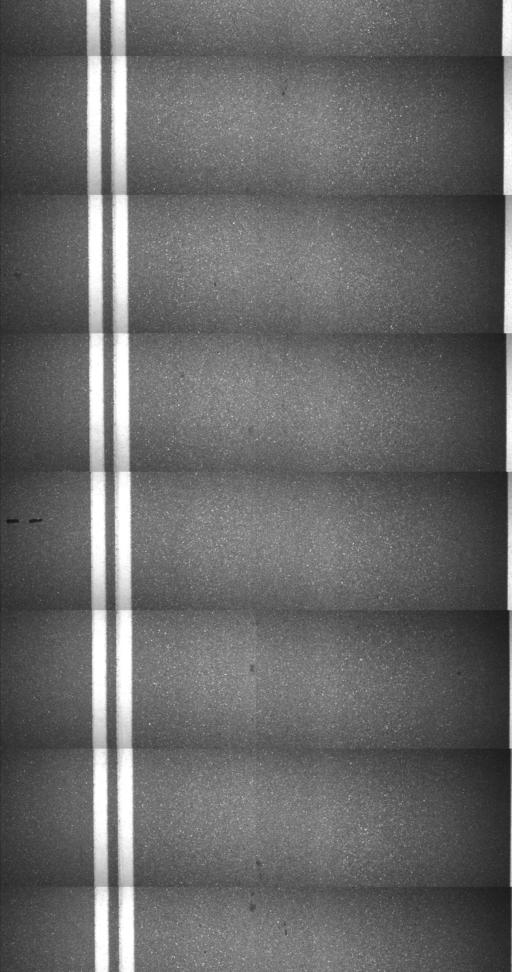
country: US
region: Vermont
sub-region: Windham County
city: Dover
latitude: 43.0336
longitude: -72.8414
